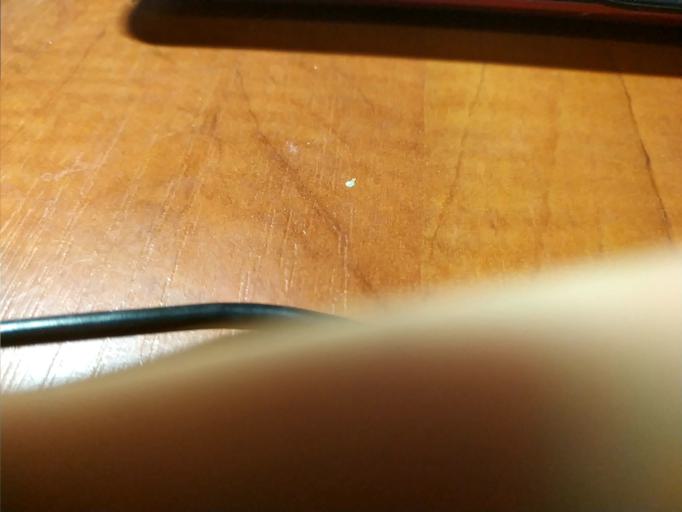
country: RU
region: Tverskaya
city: Likhoslavl'
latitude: 57.0156
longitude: 35.6157
